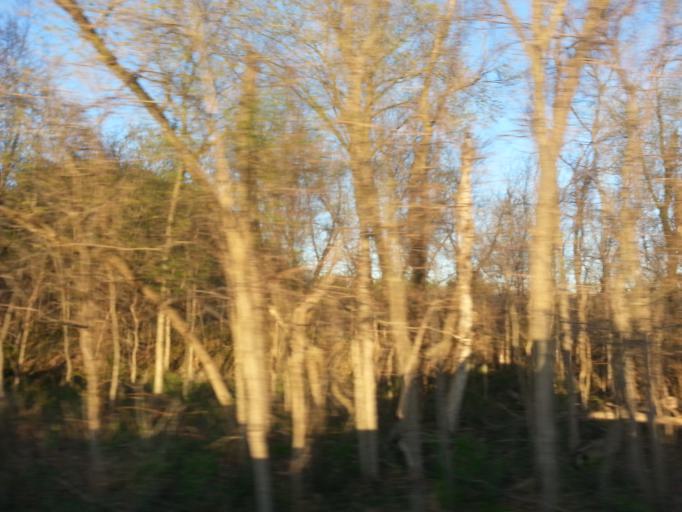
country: US
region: Wisconsin
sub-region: Pierce County
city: Prescott
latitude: 44.7695
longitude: -92.8174
